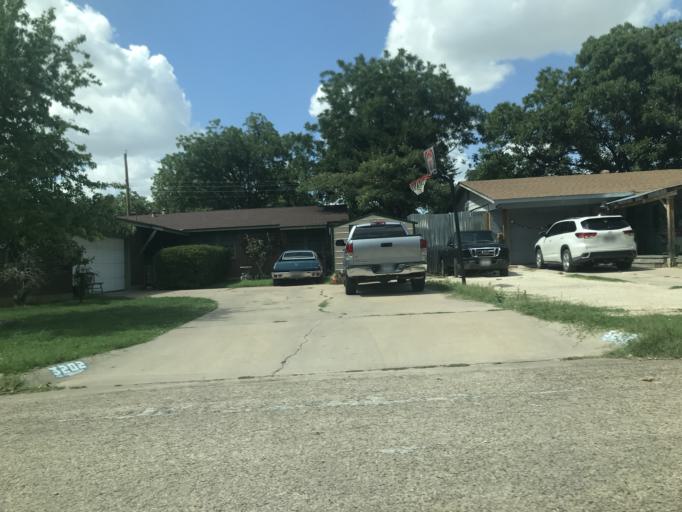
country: US
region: Texas
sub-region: Taylor County
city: Abilene
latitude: 32.4218
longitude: -99.7626
